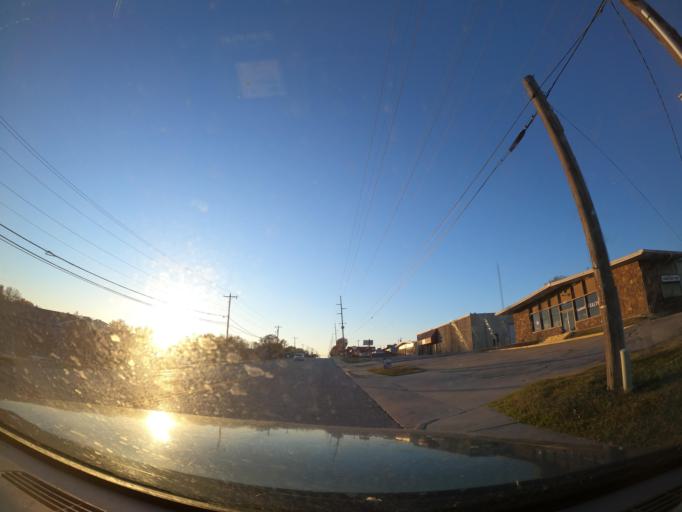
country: US
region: Oklahoma
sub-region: Tulsa County
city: Tulsa
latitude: 36.1408
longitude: -95.8982
